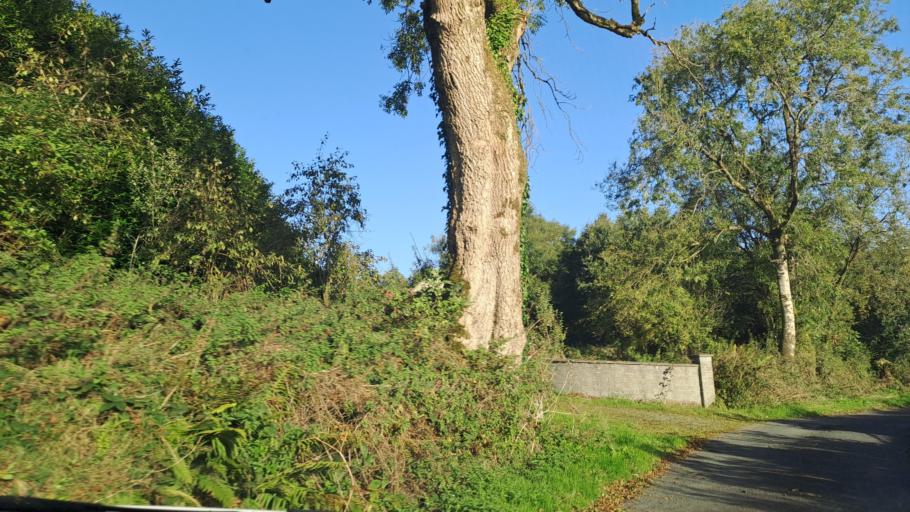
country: IE
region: Ulster
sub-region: An Cabhan
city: Kingscourt
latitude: 53.9809
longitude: -6.8497
